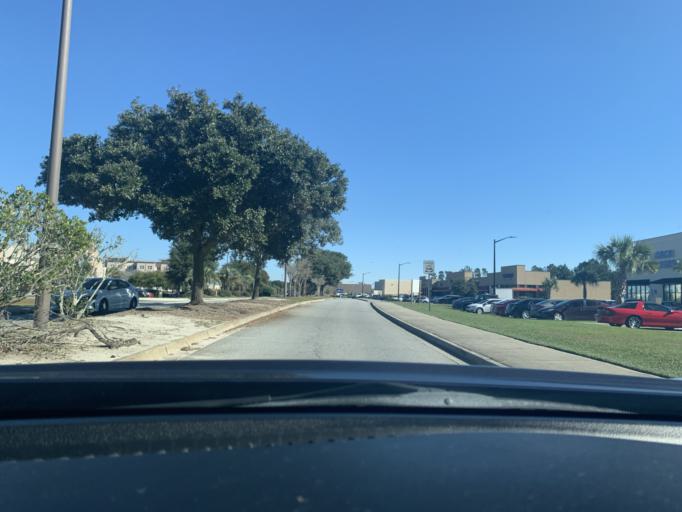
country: US
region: Georgia
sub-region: Chatham County
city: Pooler
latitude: 32.1399
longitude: -81.2559
